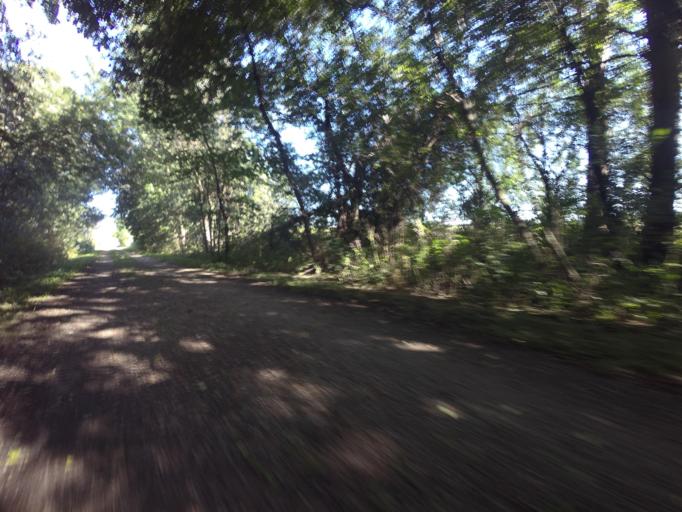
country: CA
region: Ontario
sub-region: Wellington County
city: Guelph
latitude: 43.6585
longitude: -80.4266
